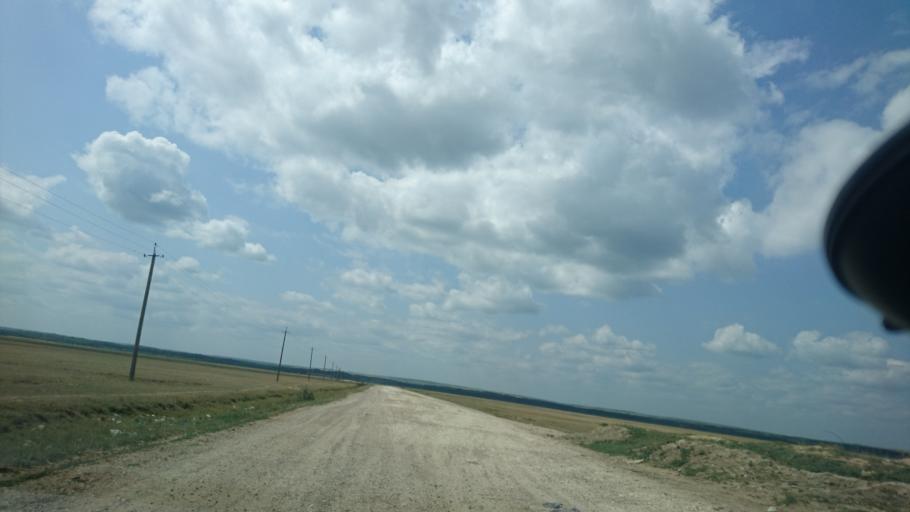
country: RO
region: Iasi
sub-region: Comuna Bivolari
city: Bivolari
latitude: 47.5591
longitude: 27.4818
